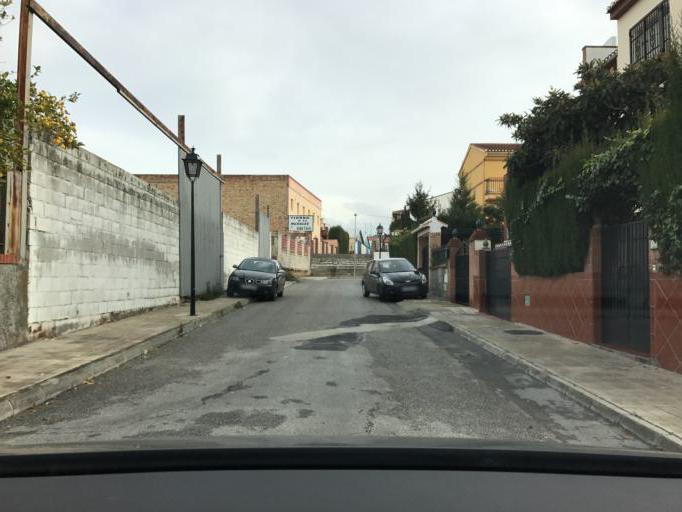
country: ES
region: Andalusia
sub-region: Provincia de Granada
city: Jun
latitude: 37.2171
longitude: -3.5966
